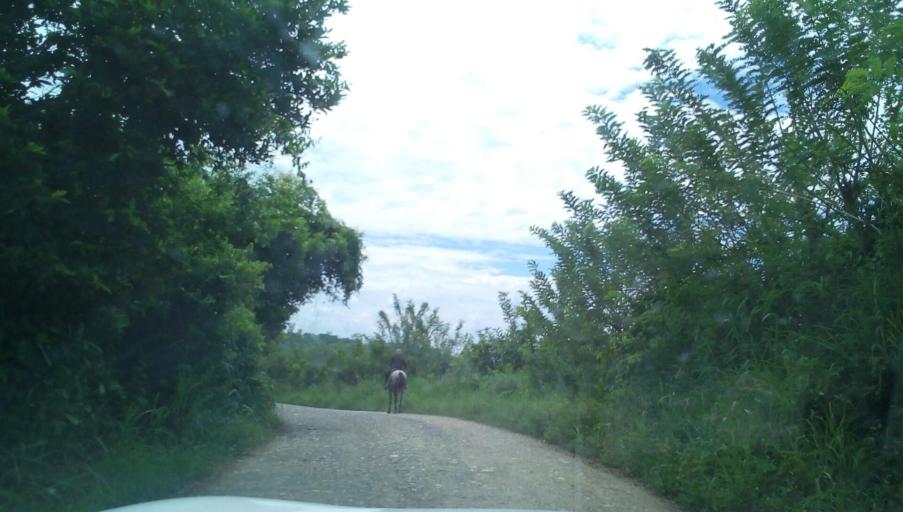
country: MX
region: Veracruz
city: Tepetzintla
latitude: 21.1449
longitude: -97.8553
